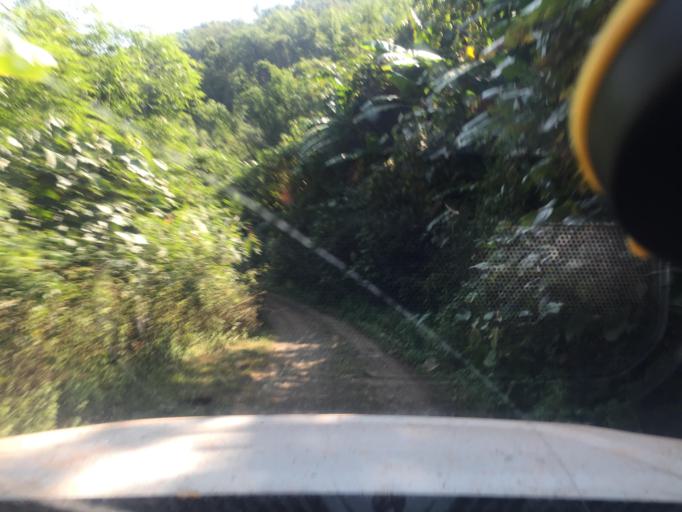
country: LA
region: Phongsali
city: Phongsali
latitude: 21.7038
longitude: 102.3970
